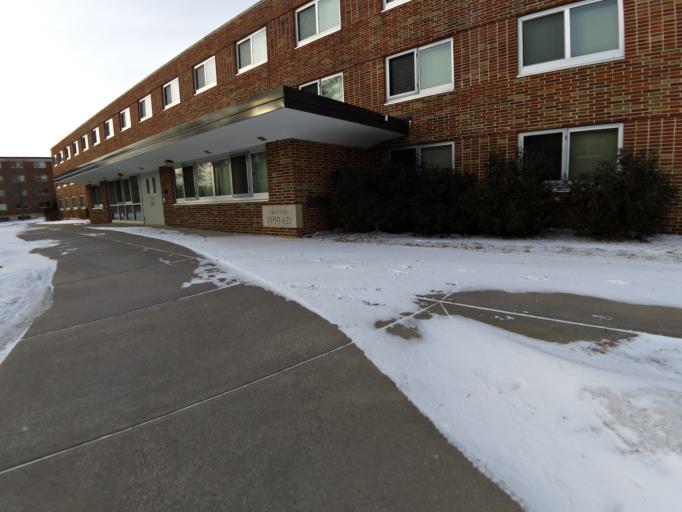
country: US
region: Wisconsin
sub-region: Pierce County
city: River Falls
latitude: 44.8534
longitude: -92.6272
